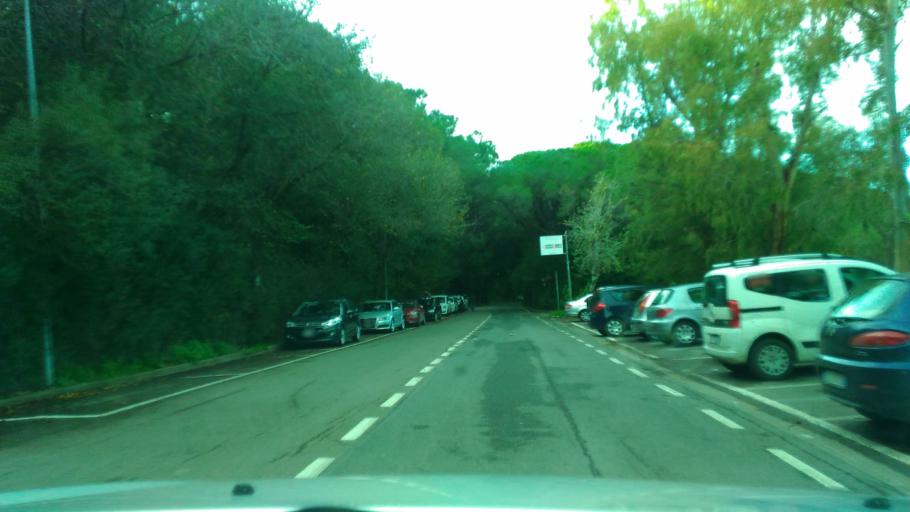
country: IT
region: Tuscany
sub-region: Provincia di Livorno
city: Cecina
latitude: 43.2925
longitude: 10.5058
